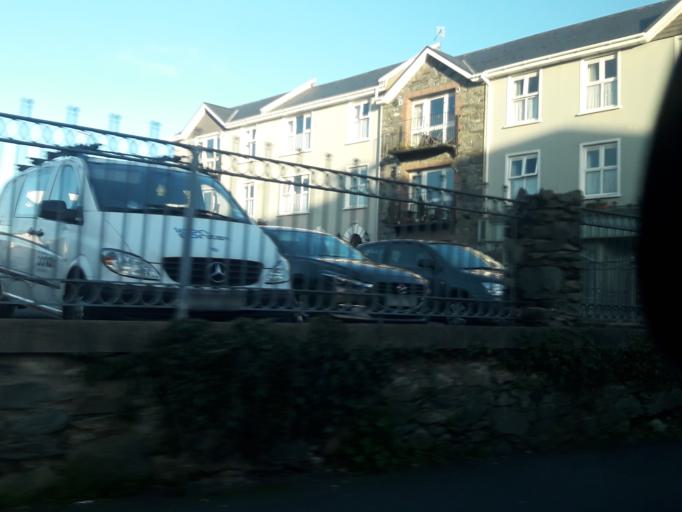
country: IE
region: Munster
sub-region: Ciarrai
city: Cill Airne
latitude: 52.0608
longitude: -9.5119
